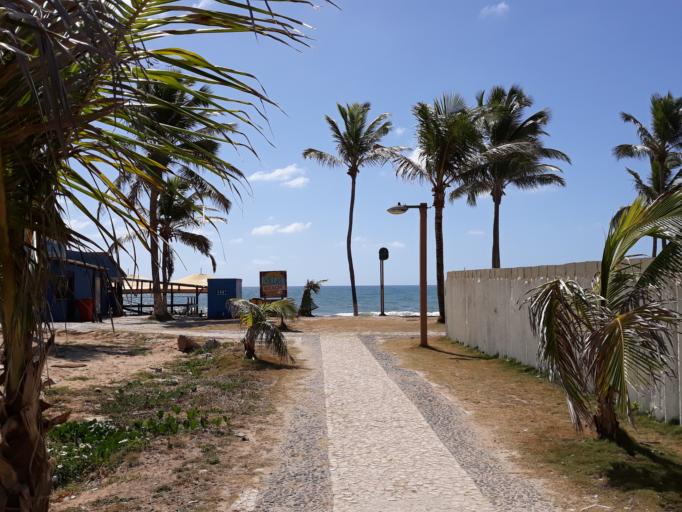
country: BR
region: Bahia
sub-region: Lauro De Freitas
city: Lauro de Freitas
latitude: -12.8900
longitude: -38.2888
